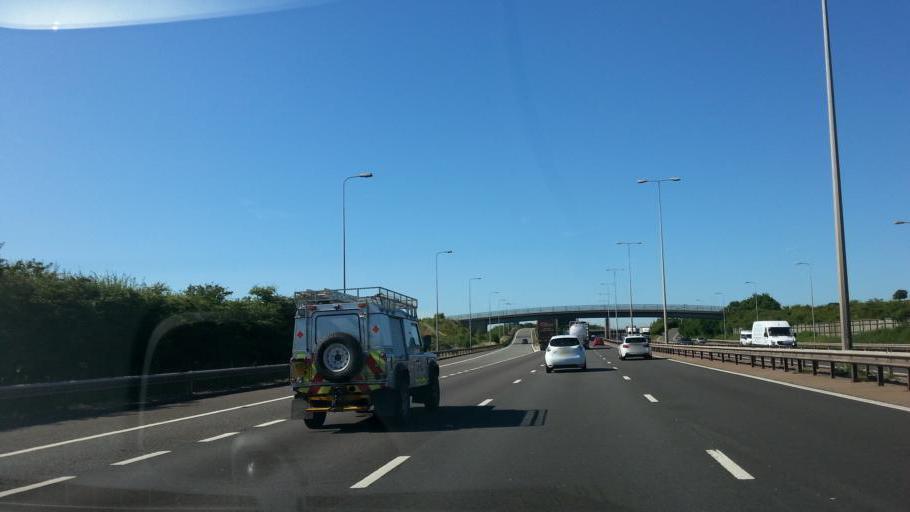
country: GB
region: England
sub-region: Worcestershire
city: Worcester
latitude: 52.1739
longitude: -2.1760
